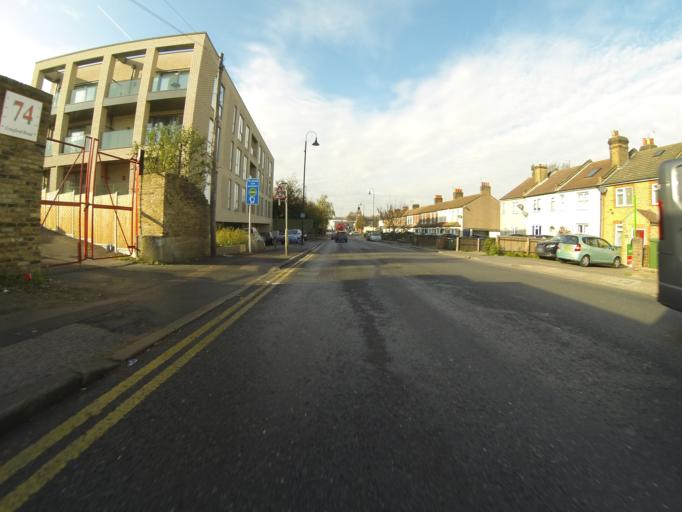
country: GB
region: England
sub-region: Greater London
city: Erith
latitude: 51.4498
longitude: 0.1841
